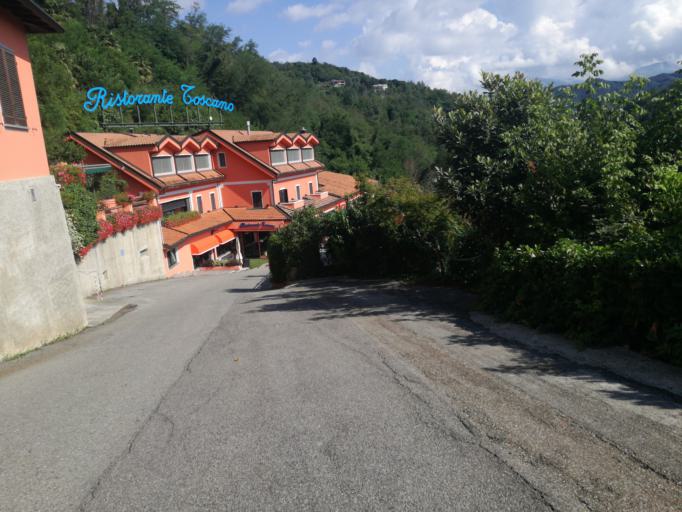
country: IT
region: Lombardy
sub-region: Provincia di Lecco
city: Paderno d'Adda
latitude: 45.6835
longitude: 9.4496
